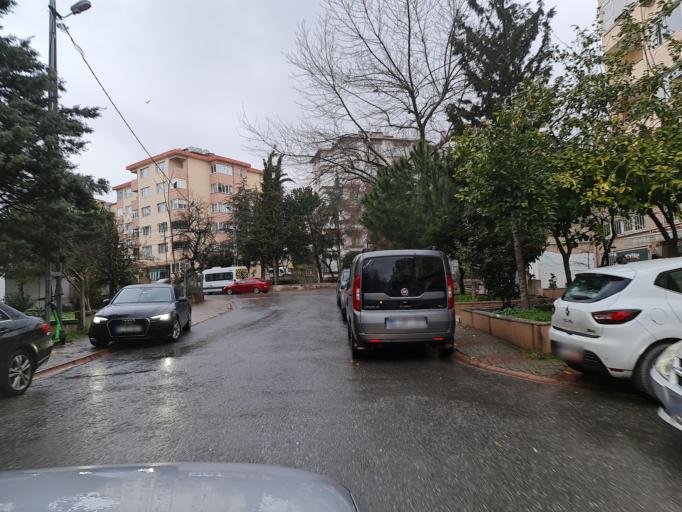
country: TR
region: Istanbul
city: Umraniye
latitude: 41.0101
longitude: 29.1019
